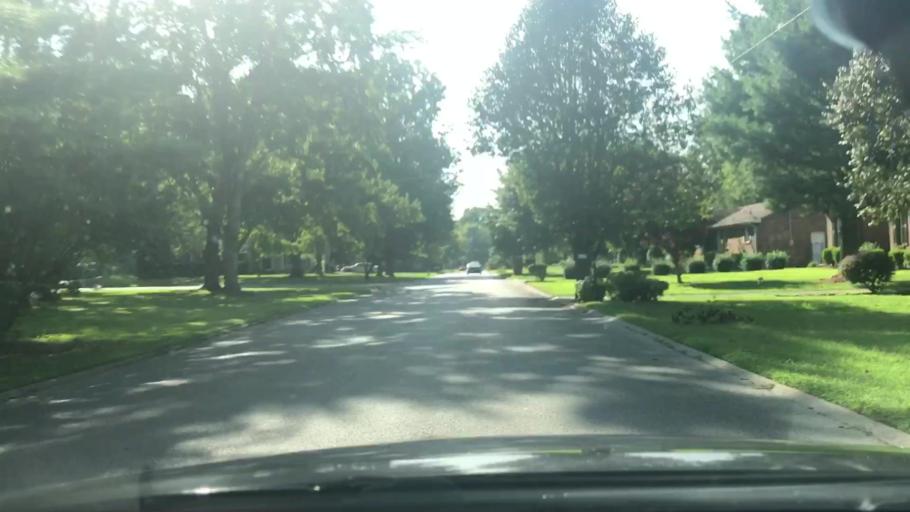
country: US
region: Tennessee
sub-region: Williamson County
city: Franklin
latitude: 35.9307
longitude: -86.8832
